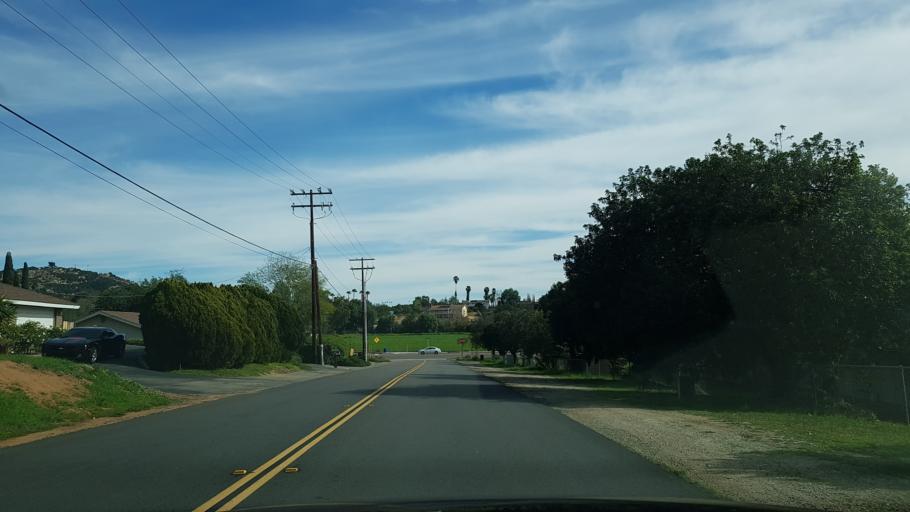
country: US
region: California
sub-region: San Diego County
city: Escondido
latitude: 33.1186
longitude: -117.0510
